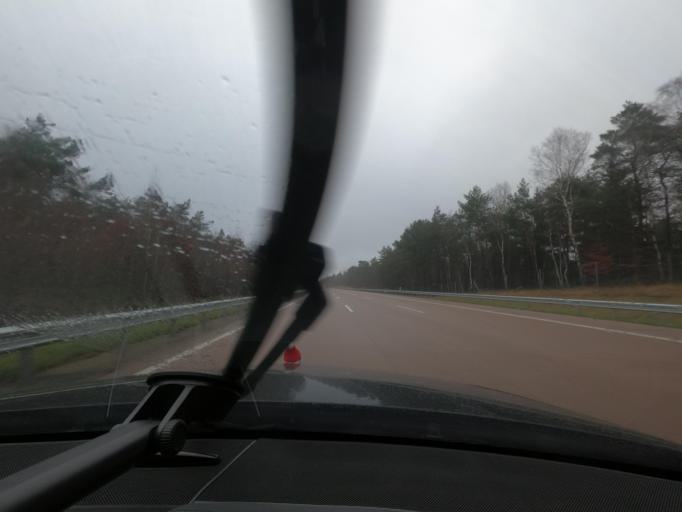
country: DE
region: Lower Saxony
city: Bispingen
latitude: 53.0425
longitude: 9.9515
